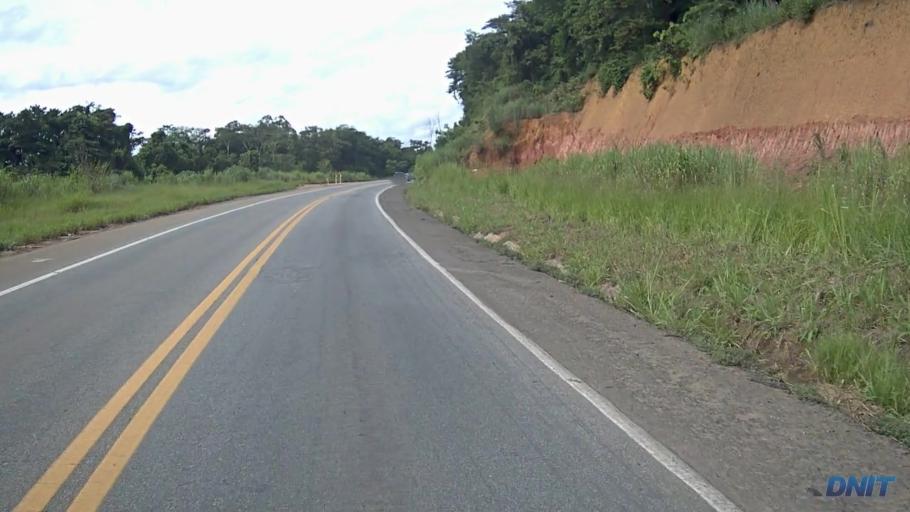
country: BR
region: Minas Gerais
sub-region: Ipaba
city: Ipaba
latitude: -19.3435
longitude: -42.4317
